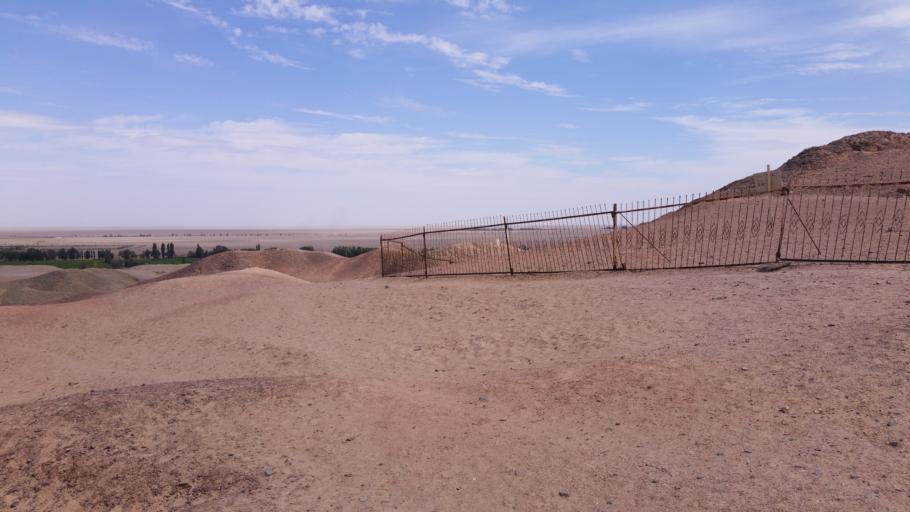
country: CN
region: Heilongjiang Sheng
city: Hongliuwan
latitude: 39.9271
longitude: 94.0585
